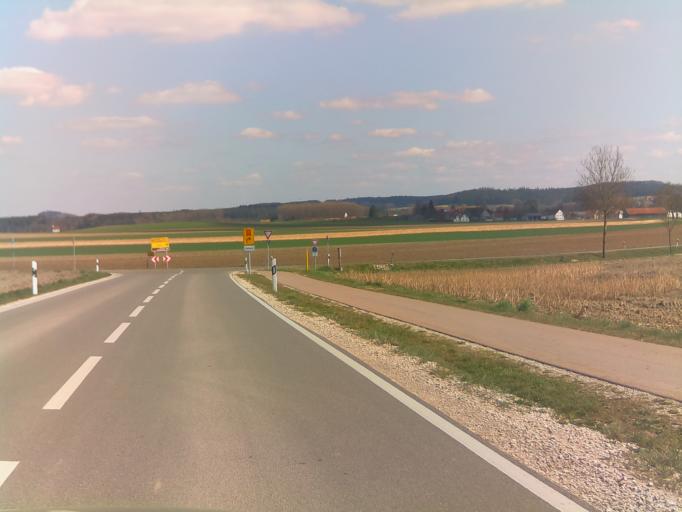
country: DE
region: Bavaria
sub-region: Swabia
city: Inchenhofen
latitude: 48.4885
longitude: 11.1150
